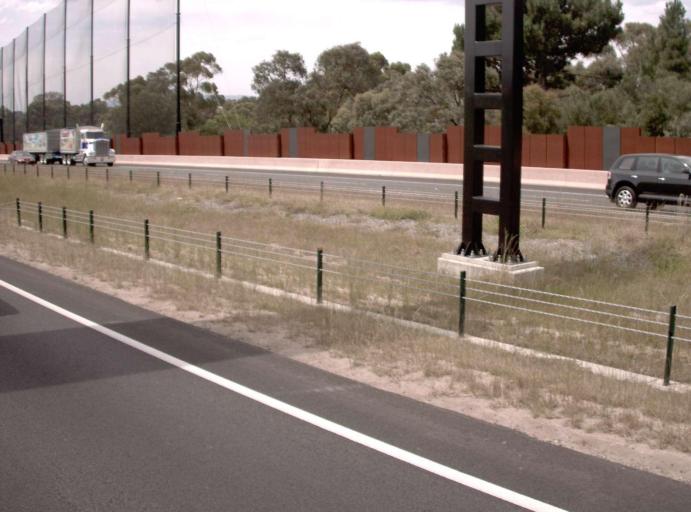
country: AU
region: Victoria
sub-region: Frankston
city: Frankston North
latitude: -38.1275
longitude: 145.1722
